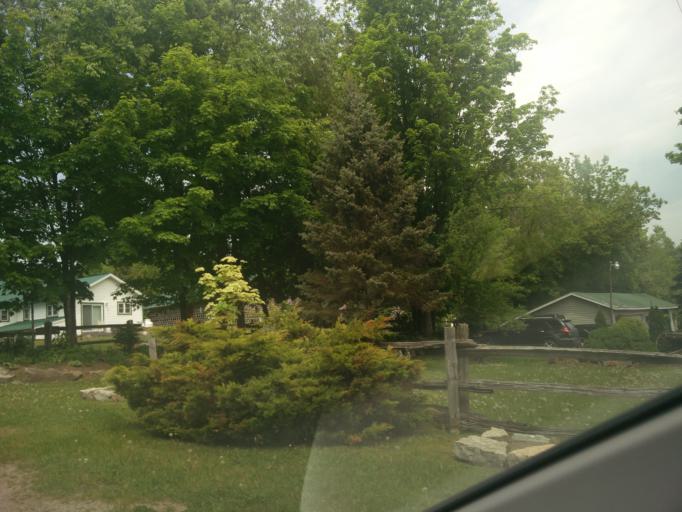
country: CA
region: Ontario
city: Perth
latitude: 44.6815
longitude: -76.4057
